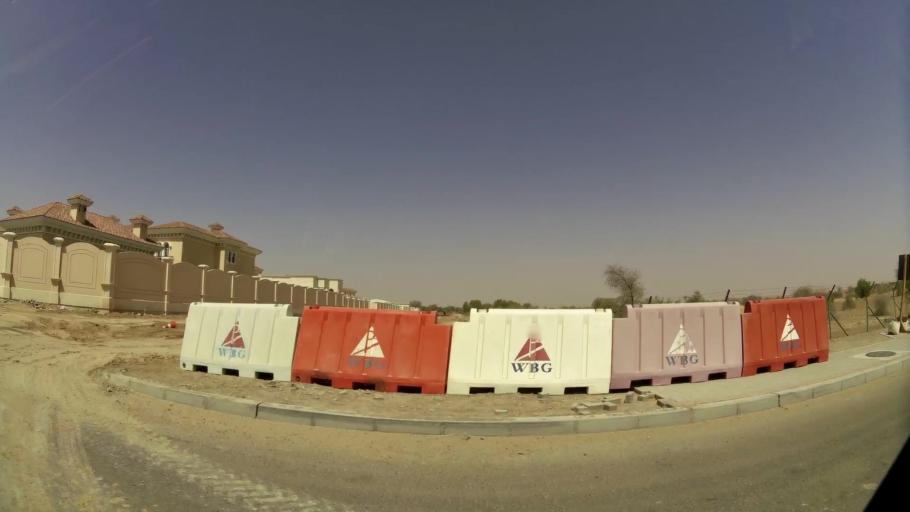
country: OM
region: Al Buraimi
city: Al Buraymi
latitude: 24.2891
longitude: 55.7582
